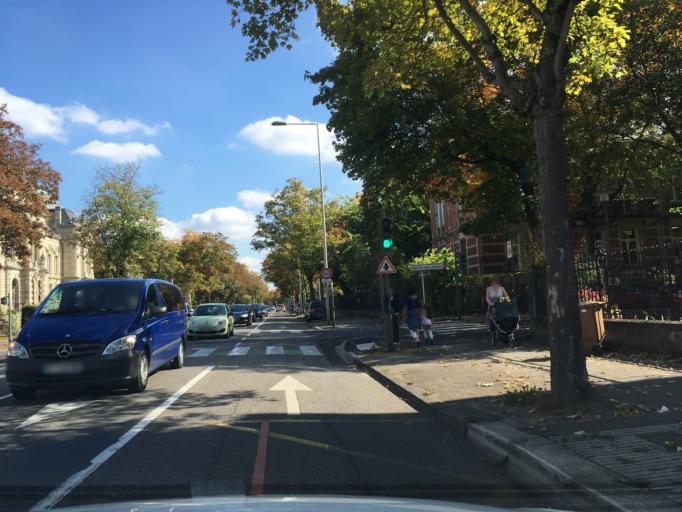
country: FR
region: Alsace
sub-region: Departement du Haut-Rhin
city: Colmar
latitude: 48.0715
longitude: 7.3495
